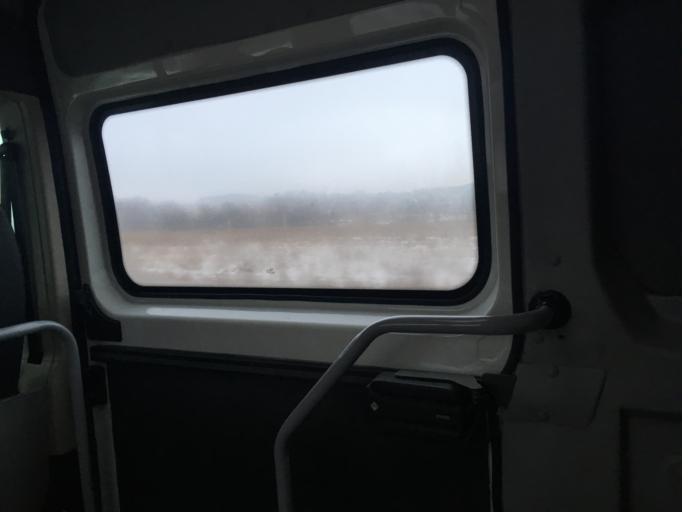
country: RU
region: Tula
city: Krapivna
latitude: 54.1146
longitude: 37.2201
